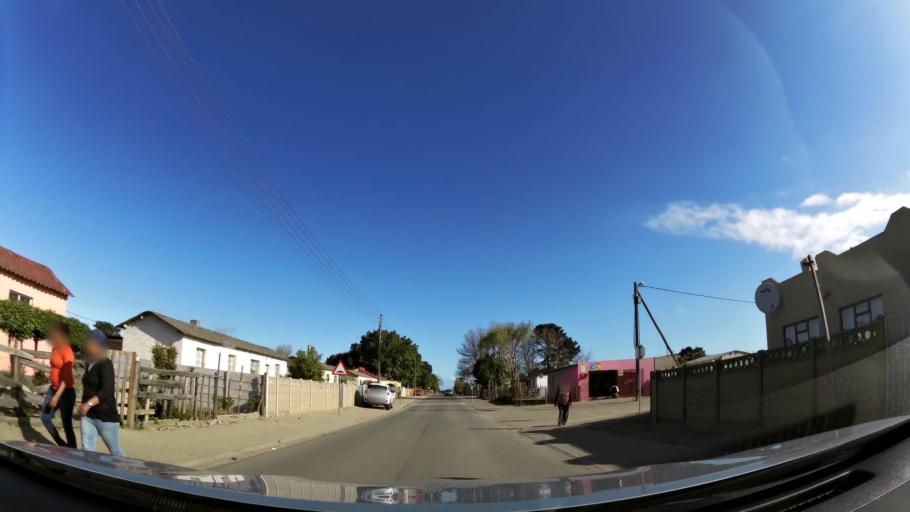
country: ZA
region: Western Cape
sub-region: Eden District Municipality
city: George
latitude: -33.9714
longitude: 22.4795
